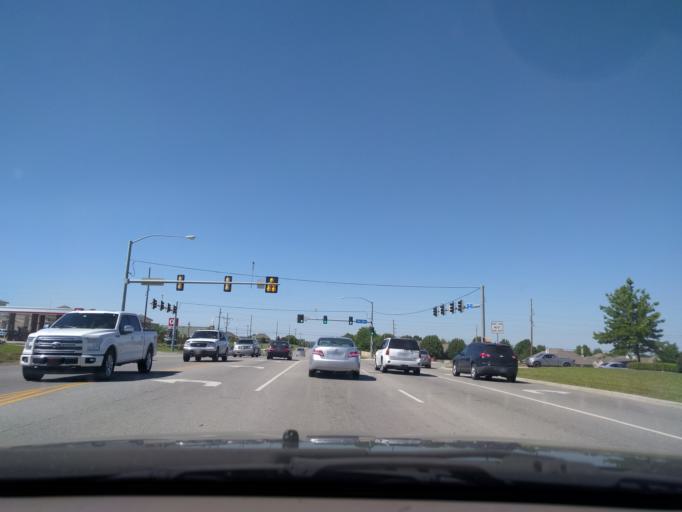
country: US
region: Oklahoma
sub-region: Tulsa County
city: Broken Arrow
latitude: 36.0667
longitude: -95.7794
